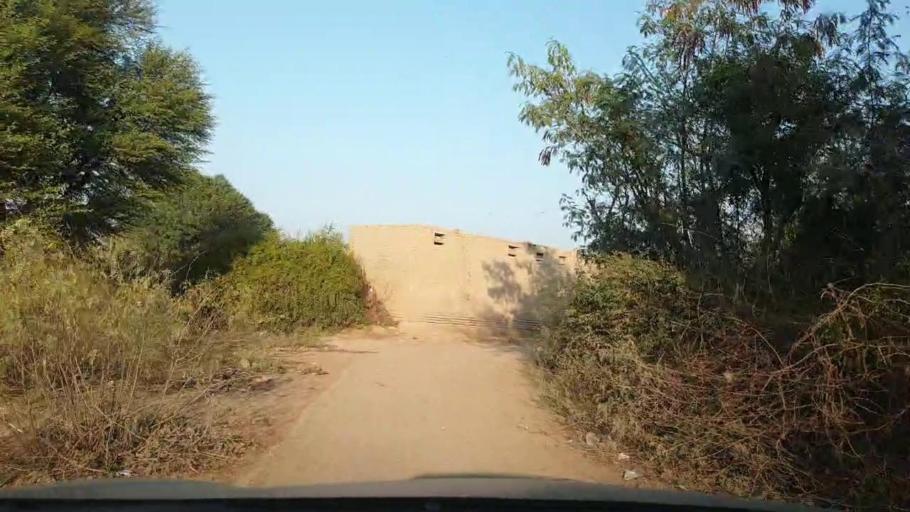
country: PK
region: Sindh
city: Tando Allahyar
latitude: 25.5658
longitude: 68.7903
